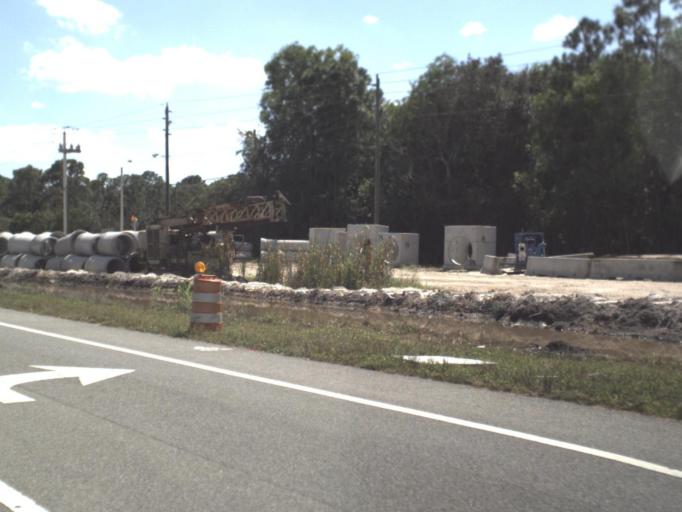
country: US
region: Florida
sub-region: Collier County
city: Lely Resort
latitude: 26.0587
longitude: -81.6919
